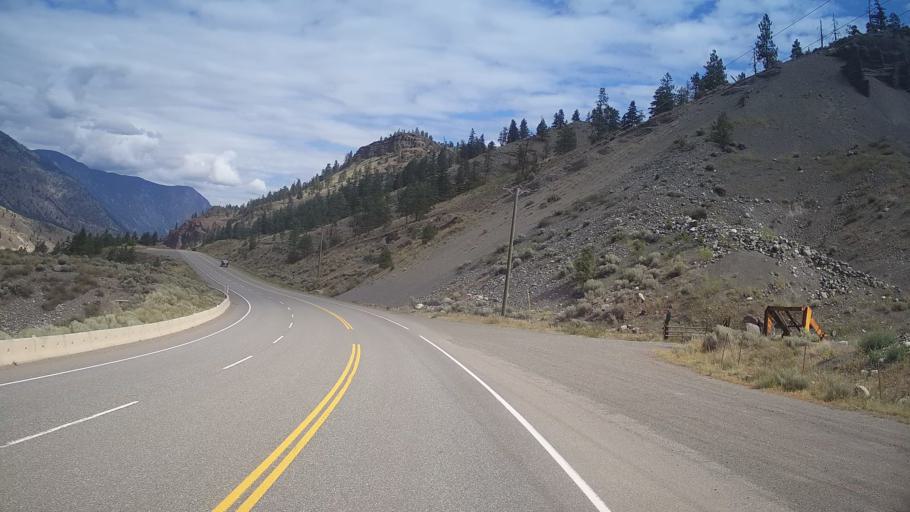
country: CA
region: British Columbia
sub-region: Thompson-Nicola Regional District
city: Ashcroft
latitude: 50.2949
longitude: -121.3930
